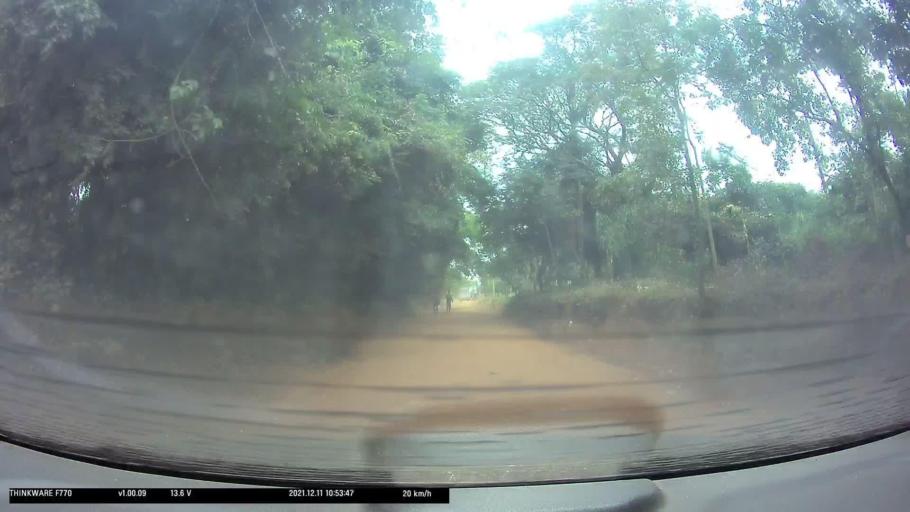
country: PY
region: Cordillera
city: Altos
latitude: -25.2930
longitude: -57.2659
